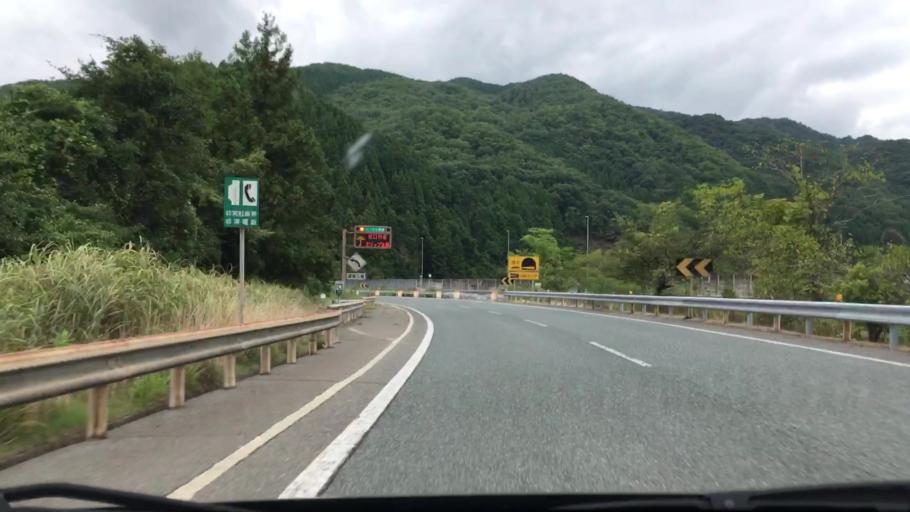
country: JP
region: Okayama
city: Niimi
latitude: 35.0074
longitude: 133.4815
